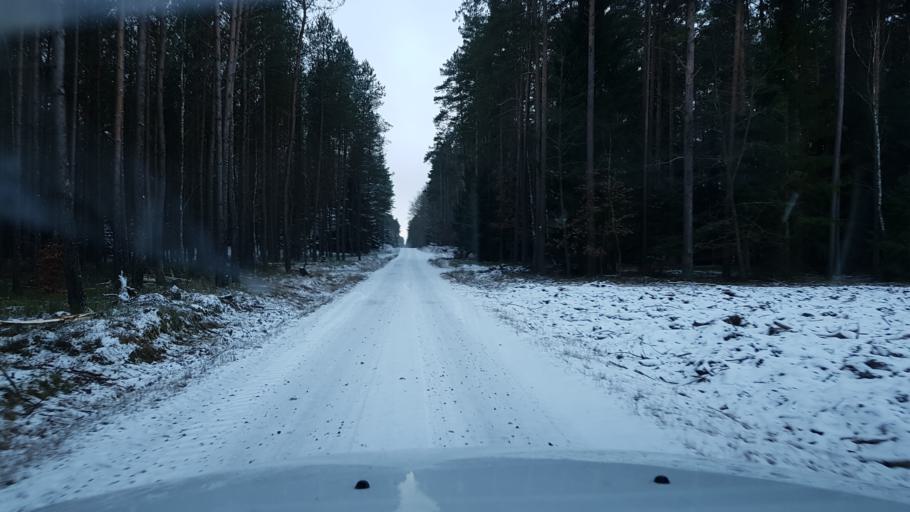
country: PL
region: West Pomeranian Voivodeship
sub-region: Powiat drawski
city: Wierzchowo
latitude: 53.4869
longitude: 16.1701
